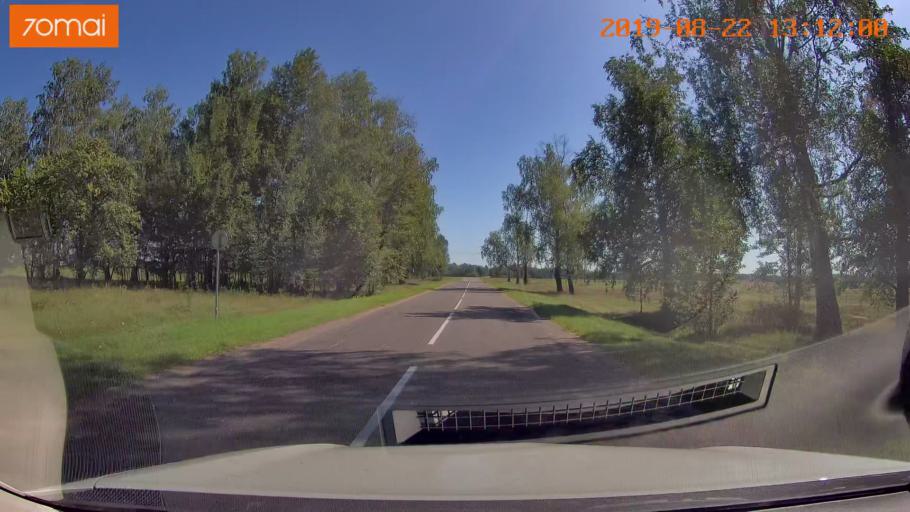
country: BY
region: Minsk
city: Prawdzinski
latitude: 53.2731
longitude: 27.8561
